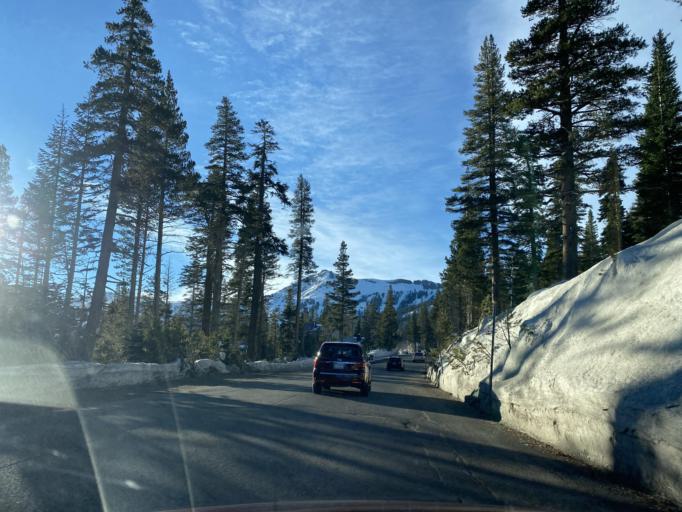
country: US
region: California
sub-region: El Dorado County
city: South Lake Tahoe
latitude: 38.6959
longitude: -120.0758
